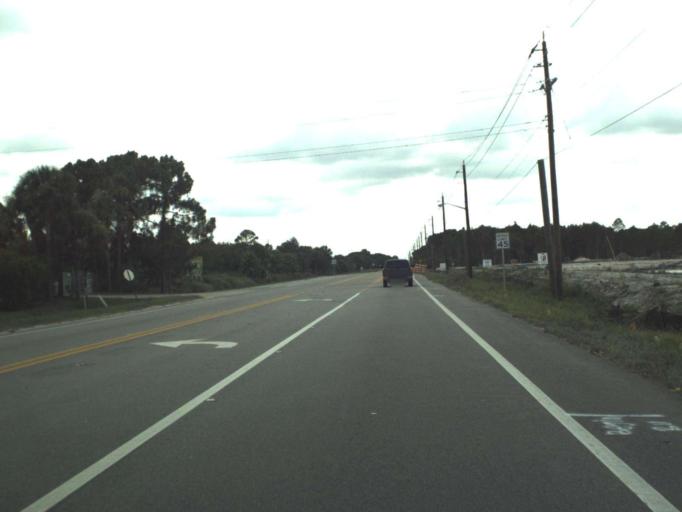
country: US
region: Florida
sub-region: Brevard County
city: June Park
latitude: 28.1213
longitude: -80.6794
